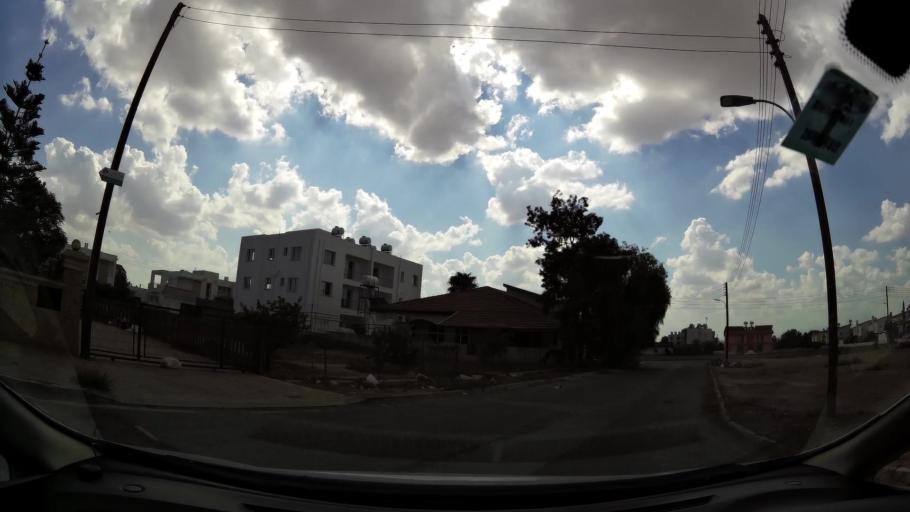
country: CY
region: Lefkosia
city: Nicosia
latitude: 35.2109
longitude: 33.3823
